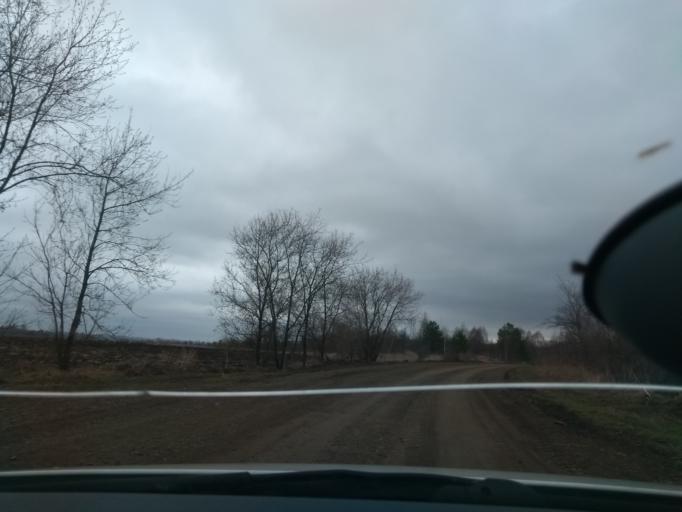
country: RU
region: Perm
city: Orda
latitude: 57.2475
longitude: 56.6123
